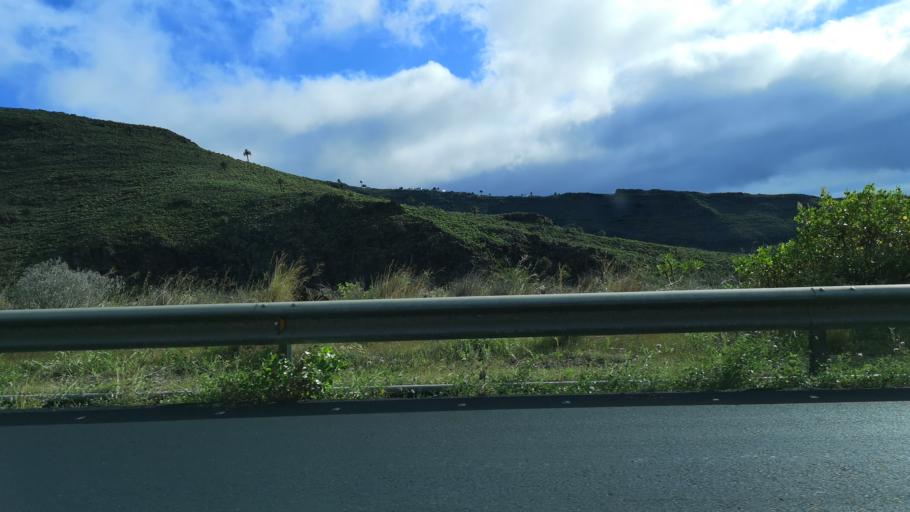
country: ES
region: Canary Islands
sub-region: Provincia de Santa Cruz de Tenerife
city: Alajero
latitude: 28.0683
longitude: -17.2065
